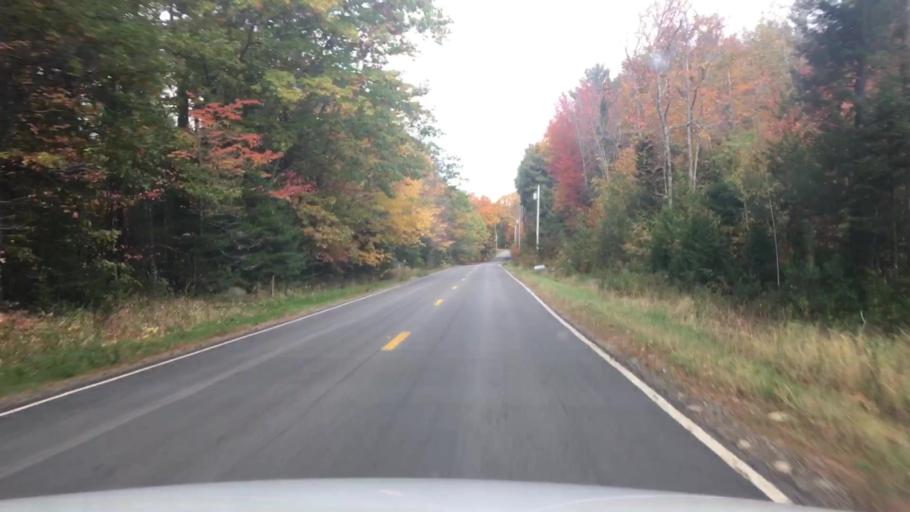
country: US
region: Maine
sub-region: Waldo County
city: Searsmont
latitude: 44.4168
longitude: -69.1396
